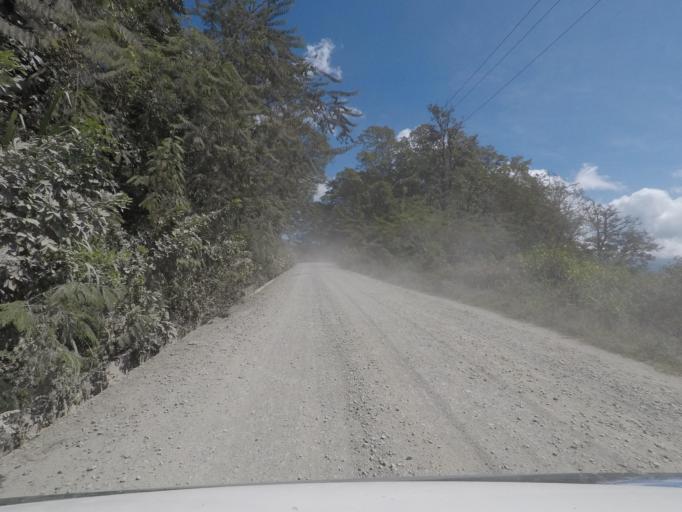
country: TL
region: Ermera
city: Gleno
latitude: -8.7458
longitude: 125.3927
